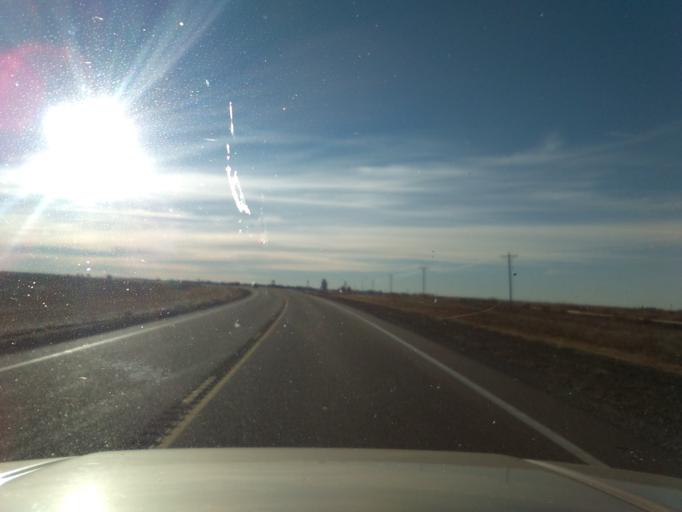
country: US
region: Kansas
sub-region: Sheridan County
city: Hoxie
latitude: 39.4804
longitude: -100.7176
